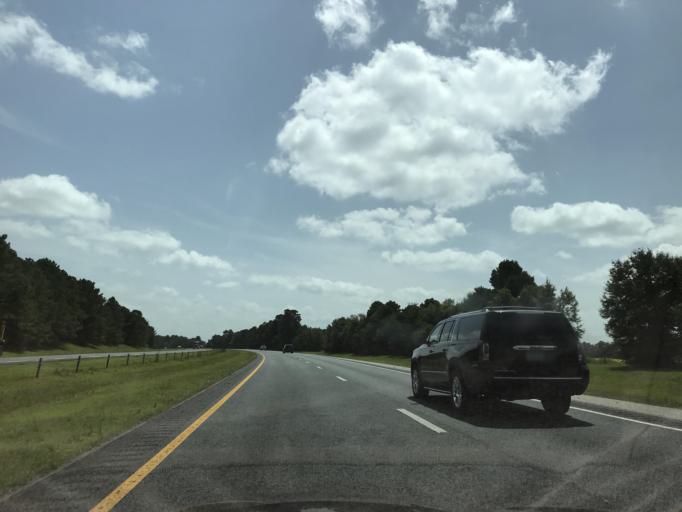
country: US
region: North Carolina
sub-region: Johnston County
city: Four Oaks
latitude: 35.3101
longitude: -78.4176
